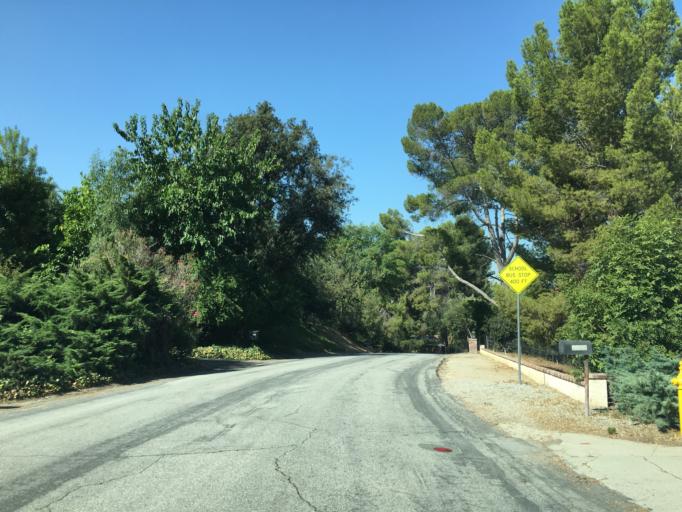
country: US
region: California
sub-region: Los Angeles County
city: Charter Oak
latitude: 34.0742
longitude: -117.8499
